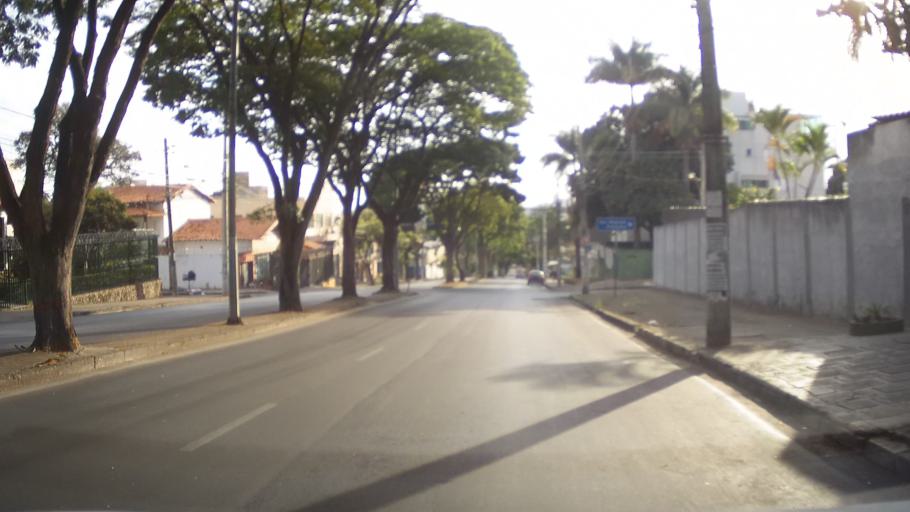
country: BR
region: Minas Gerais
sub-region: Belo Horizonte
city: Belo Horizonte
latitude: -19.8523
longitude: -43.9615
